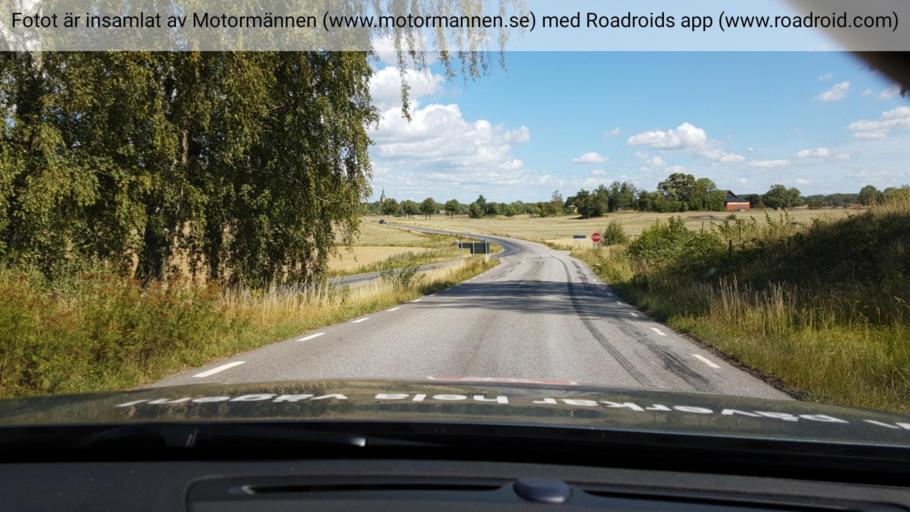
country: SE
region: Soedermanland
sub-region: Eskilstuna Kommun
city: Arla
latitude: 59.3984
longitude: 16.6766
